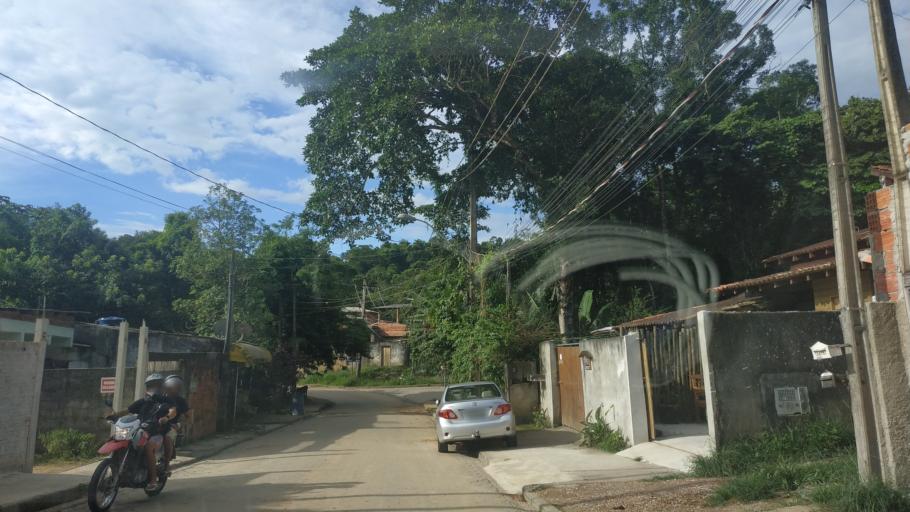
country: BR
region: Sao Paulo
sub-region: Ilhabela
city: Ilhabela
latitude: -23.8276
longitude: -45.3500
